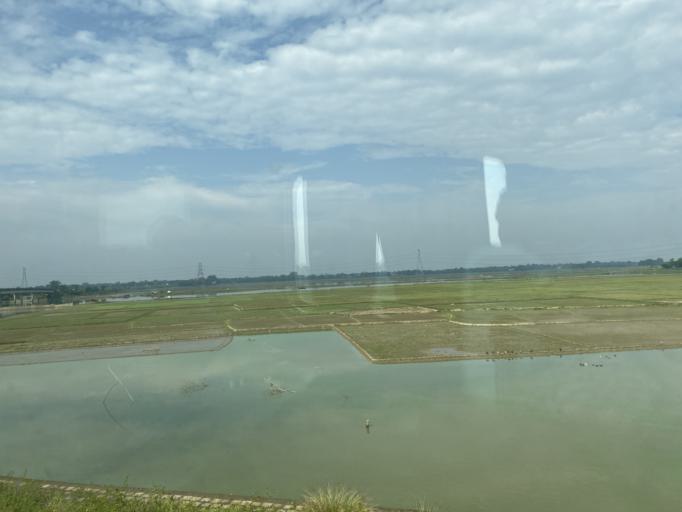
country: IN
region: Tripura
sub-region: West Tripura
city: Agartala
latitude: 23.8809
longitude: 91.2042
